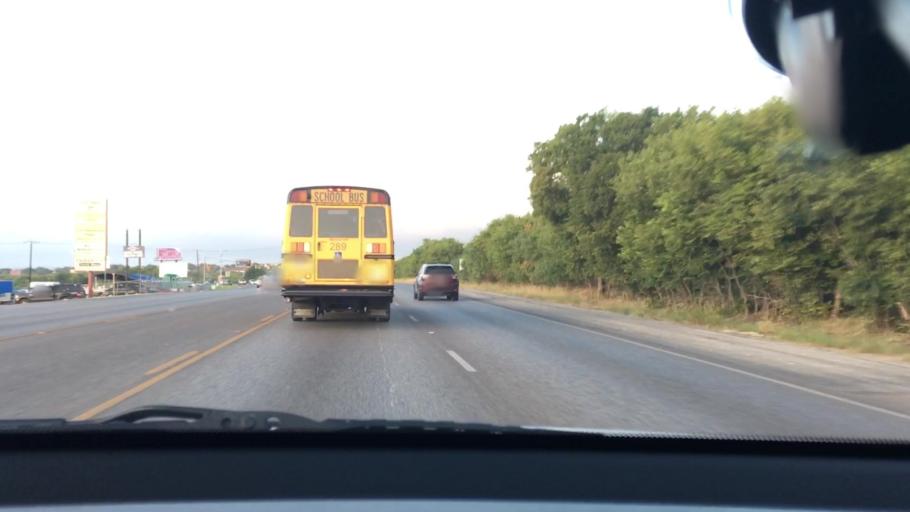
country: US
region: Texas
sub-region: Bexar County
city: Converse
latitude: 29.5281
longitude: -98.3063
